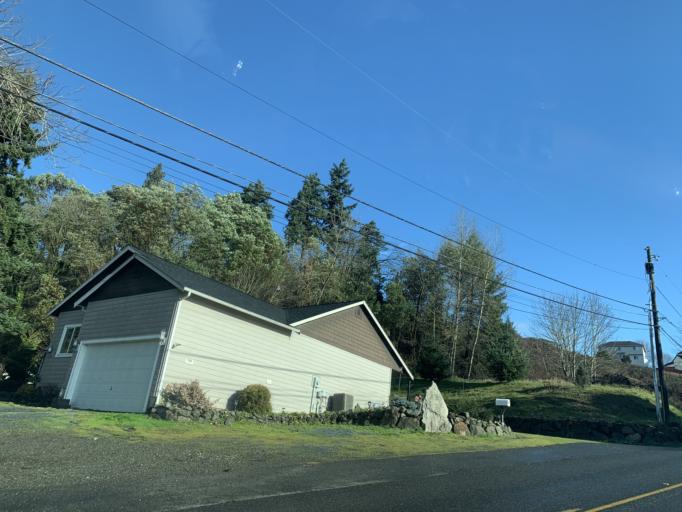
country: US
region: Washington
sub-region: Pierce County
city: Fife Heights
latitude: 47.2462
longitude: -122.3425
